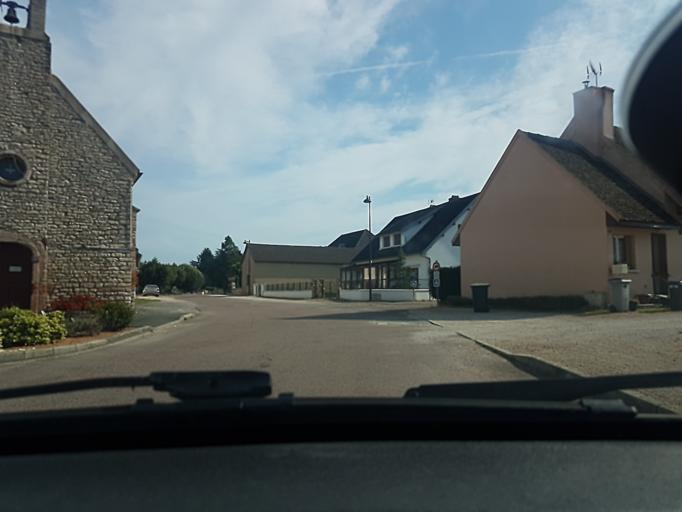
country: FR
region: Bourgogne
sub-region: Departement de Saone-et-Loire
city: Epervans
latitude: 46.7509
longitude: 4.9008
